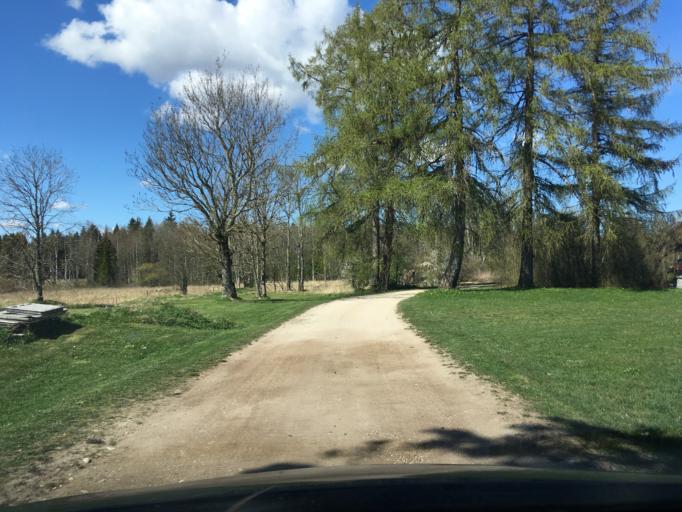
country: EE
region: Harju
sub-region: Raasiku vald
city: Raasiku
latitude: 59.2165
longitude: 25.1586
